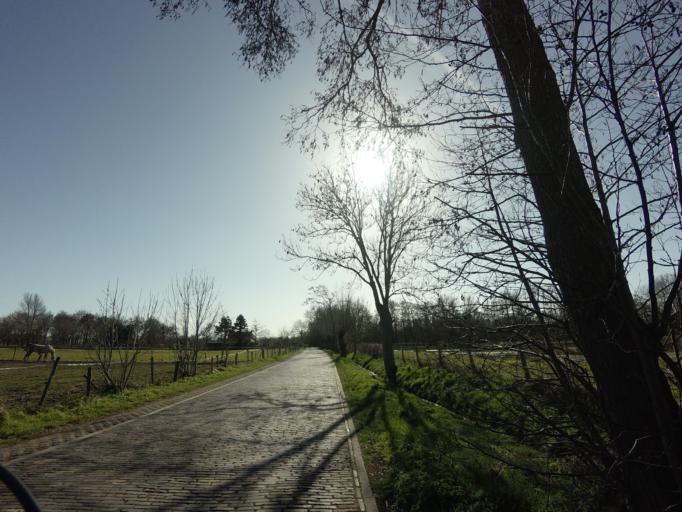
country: NL
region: Zeeland
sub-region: Schouwen-Duiveland
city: Haamstede
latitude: 51.7104
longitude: 3.7480
